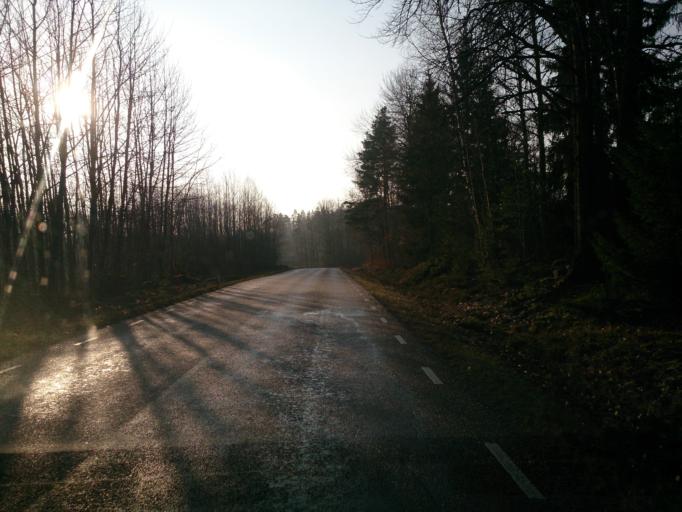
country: SE
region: OEstergoetland
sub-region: Atvidabergs Kommun
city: Atvidaberg
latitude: 58.2752
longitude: 16.0322
